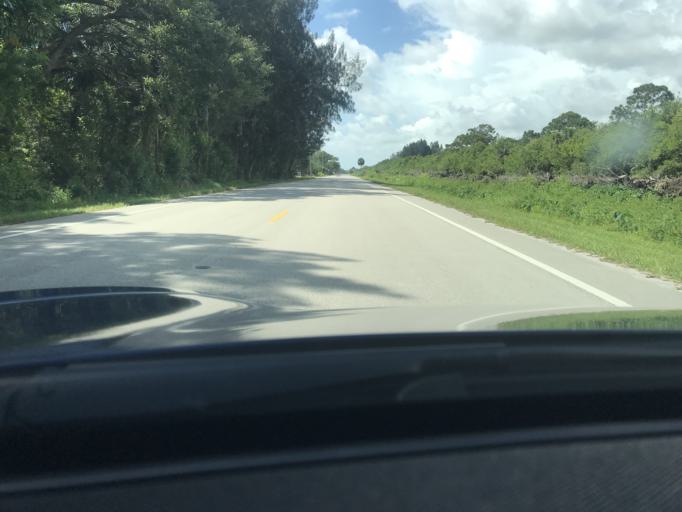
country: US
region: Florida
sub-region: Indian River County
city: Winter Beach
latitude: 27.7421
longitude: -80.4337
